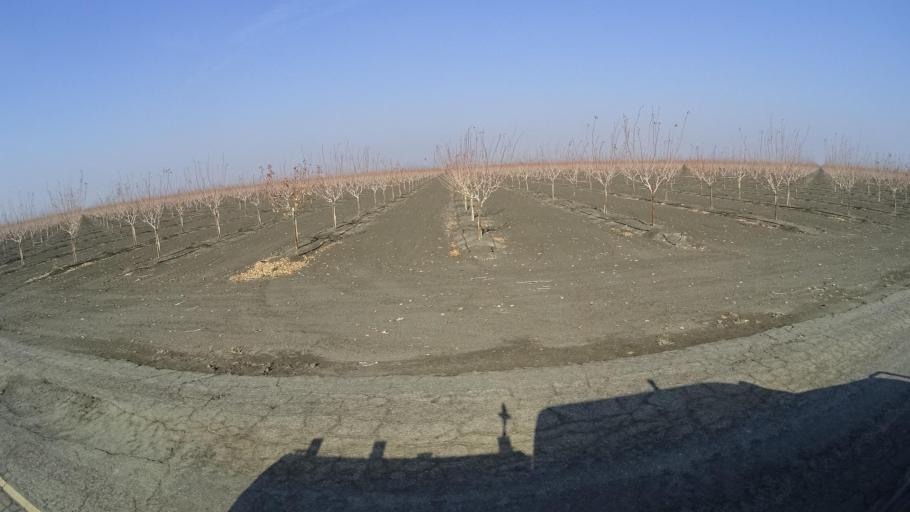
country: US
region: California
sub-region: Kern County
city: Buttonwillow
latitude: 35.3402
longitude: -119.4235
